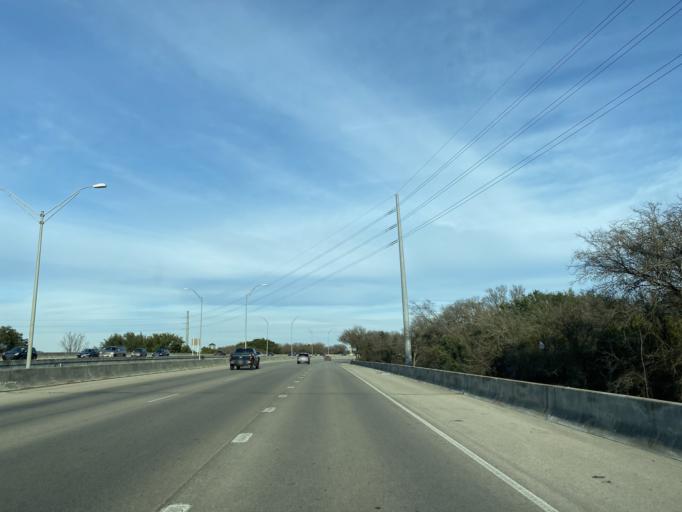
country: US
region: Texas
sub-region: Travis County
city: Shady Hollow
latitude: 30.2147
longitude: -97.8531
